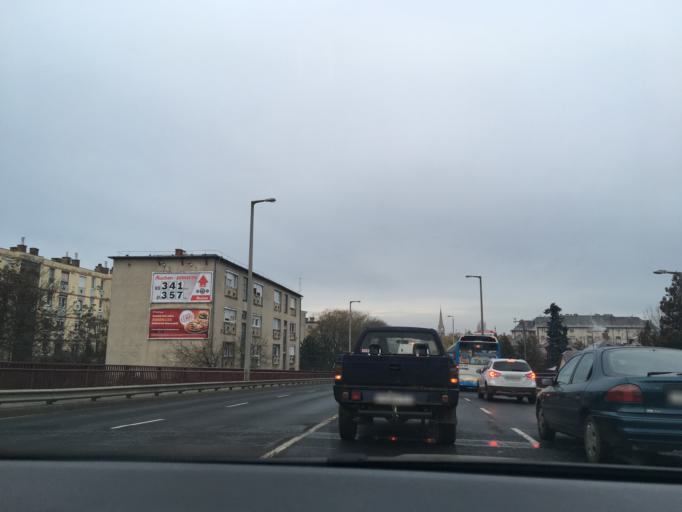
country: HU
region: Hajdu-Bihar
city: Debrecen
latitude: 47.5294
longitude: 21.6438
